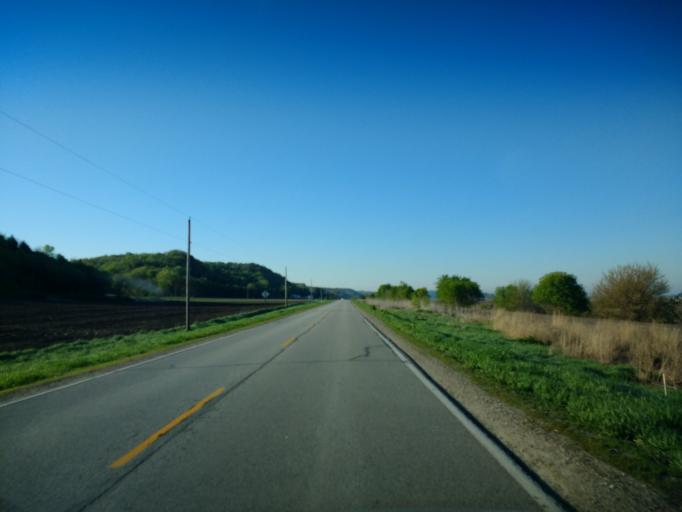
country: US
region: Iowa
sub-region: Harrison County
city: Missouri Valley
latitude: 41.4682
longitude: -95.8794
